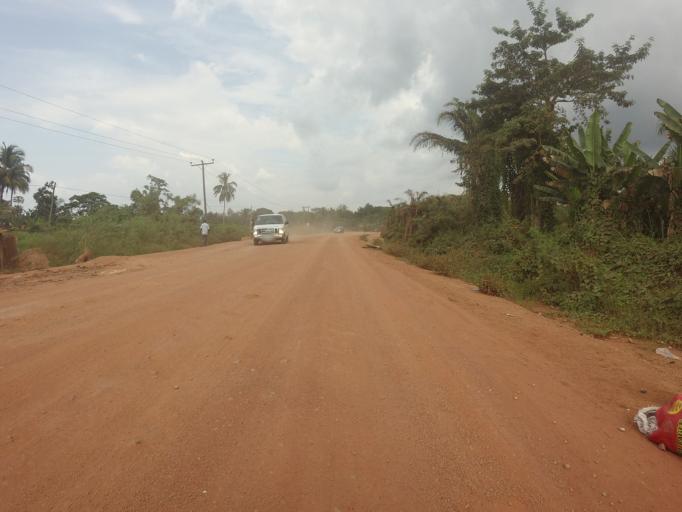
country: GH
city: Akropong
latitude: 5.9579
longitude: -0.1525
